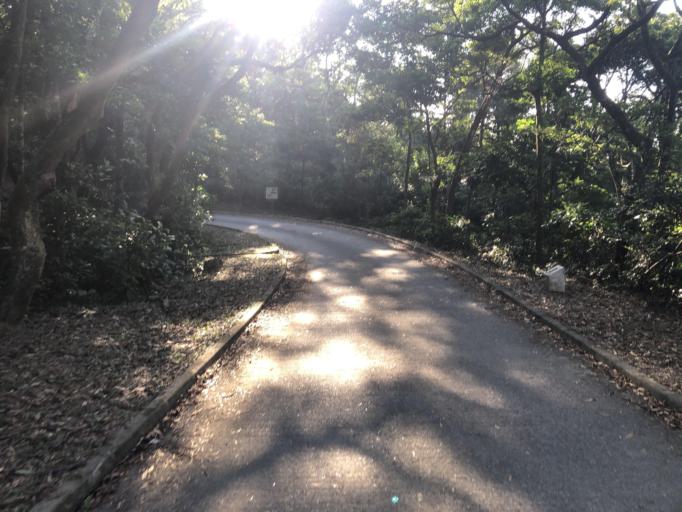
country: HK
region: Tsuen Wan
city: Tsuen Wan
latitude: 22.3983
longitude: 114.0814
